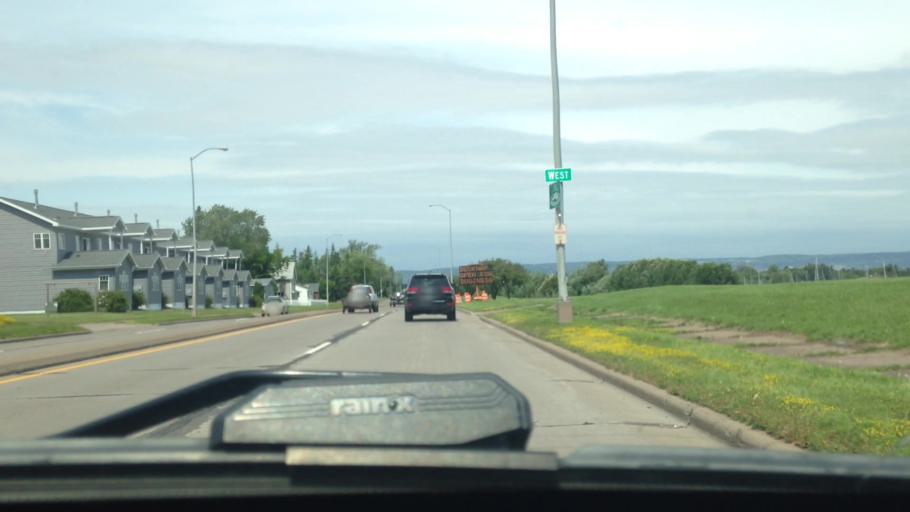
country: US
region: Wisconsin
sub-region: Douglas County
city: Superior
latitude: 46.7119
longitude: -92.0540
